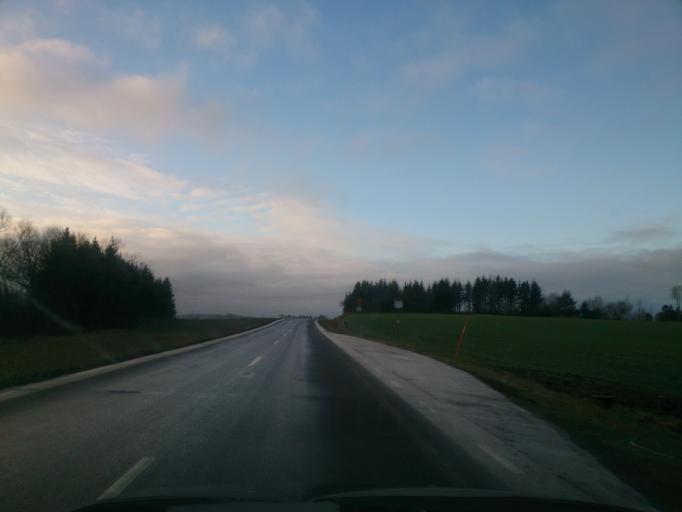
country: SE
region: OEstergoetland
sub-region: Linkopings Kommun
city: Linghem
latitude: 58.4000
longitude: 15.7851
